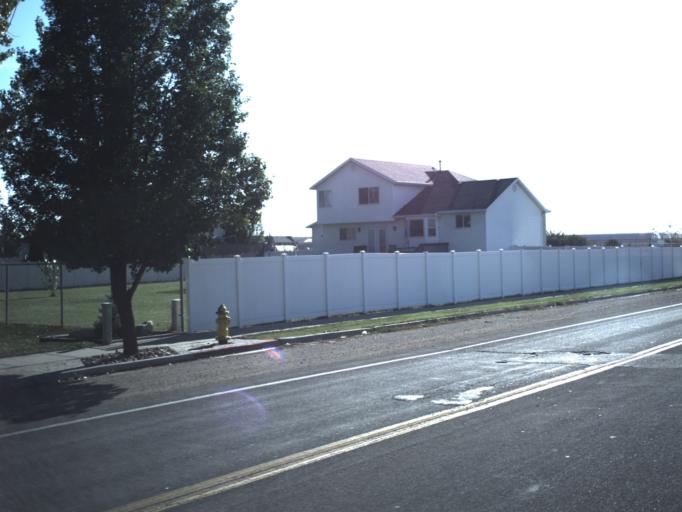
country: US
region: Utah
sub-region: Davis County
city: West Point
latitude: 41.1399
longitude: -112.0909
